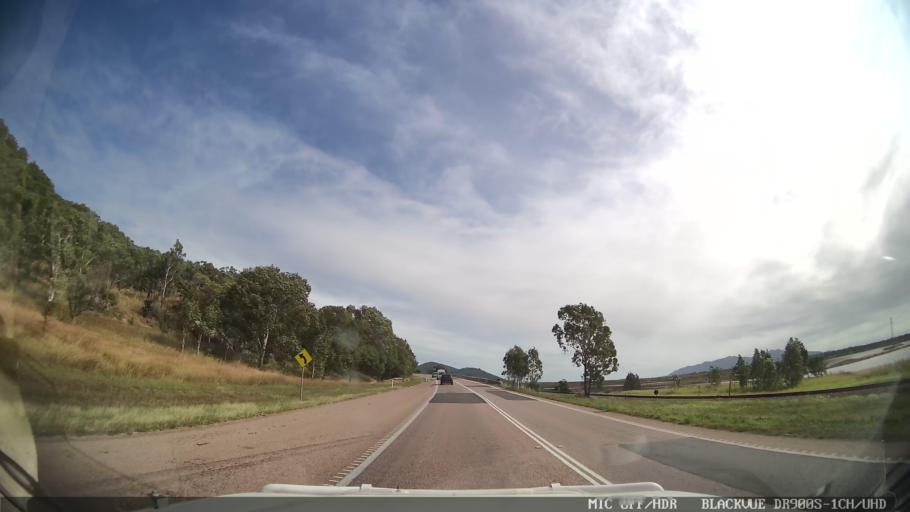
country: AU
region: Queensland
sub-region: Townsville
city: Townsville
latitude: -19.3954
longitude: 147.0206
